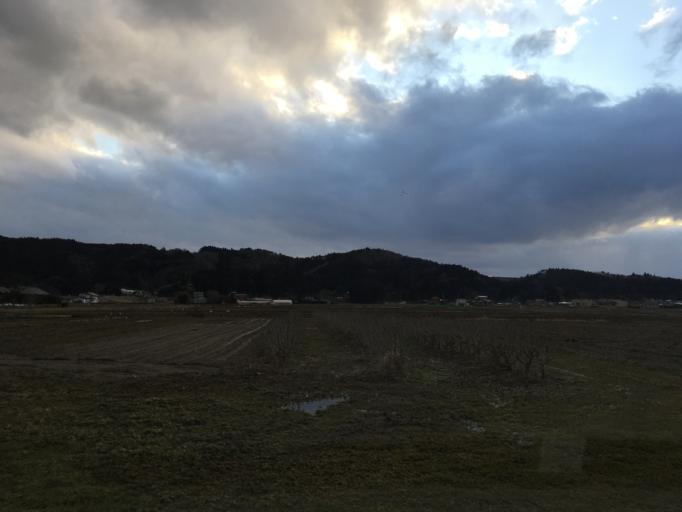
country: JP
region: Iwate
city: Ichinoseki
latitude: 38.8341
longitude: 141.2557
